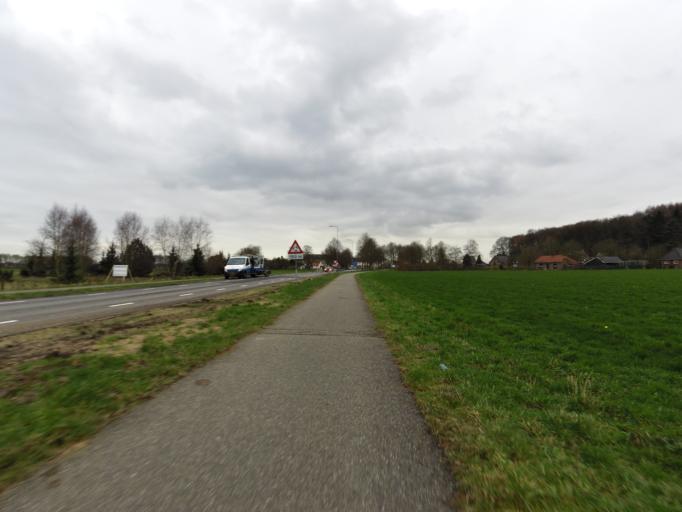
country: NL
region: Gelderland
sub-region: Gemeente Montferland
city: s-Heerenberg
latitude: 51.9118
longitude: 6.2576
